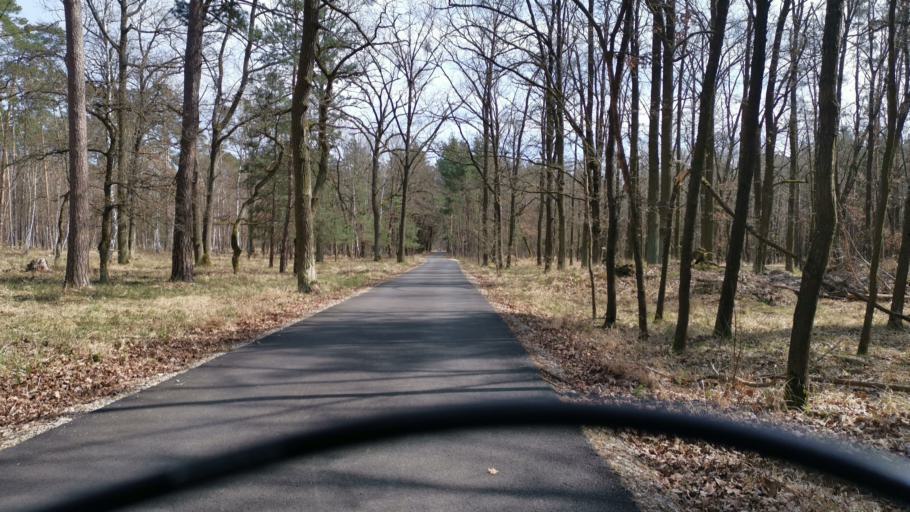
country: SK
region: Trnavsky
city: Gbely
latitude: 48.7130
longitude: 17.0594
